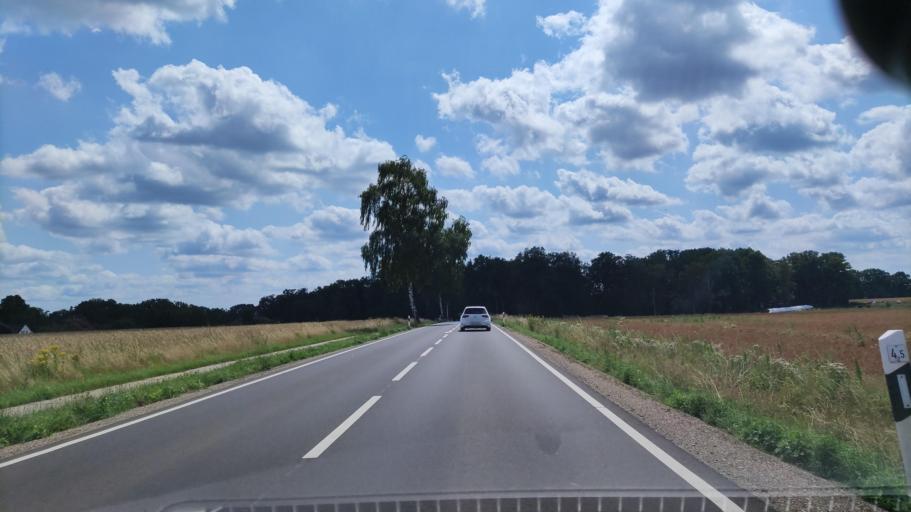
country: DE
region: Lower Saxony
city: Bomlitz
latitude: 52.9037
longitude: 9.6166
